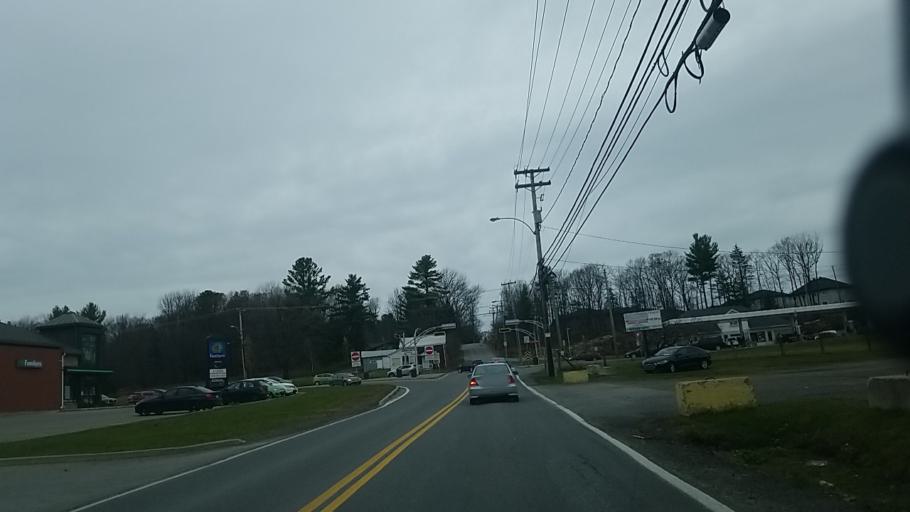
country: CA
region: Quebec
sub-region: Laurentides
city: Saint-Jerome
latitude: 45.7892
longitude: -74.0533
